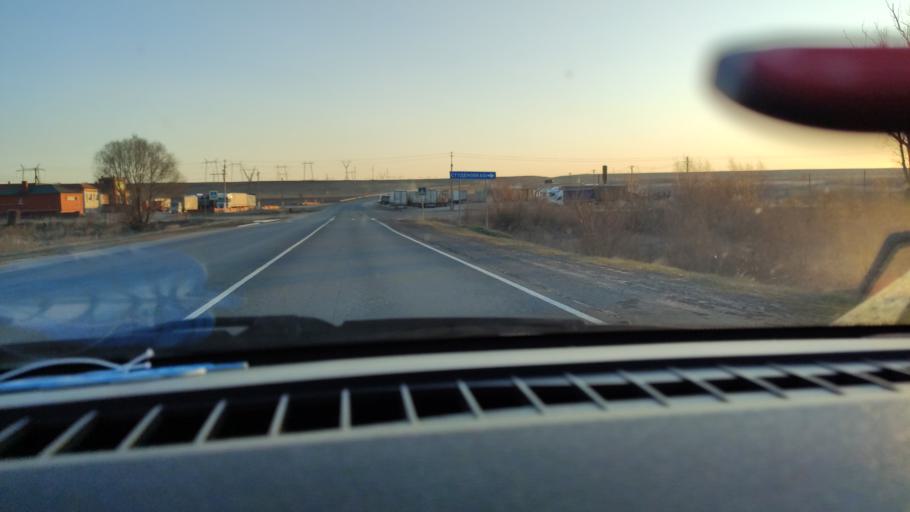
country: RU
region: Saratov
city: Sinodskoye
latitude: 51.9221
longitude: 46.5619
